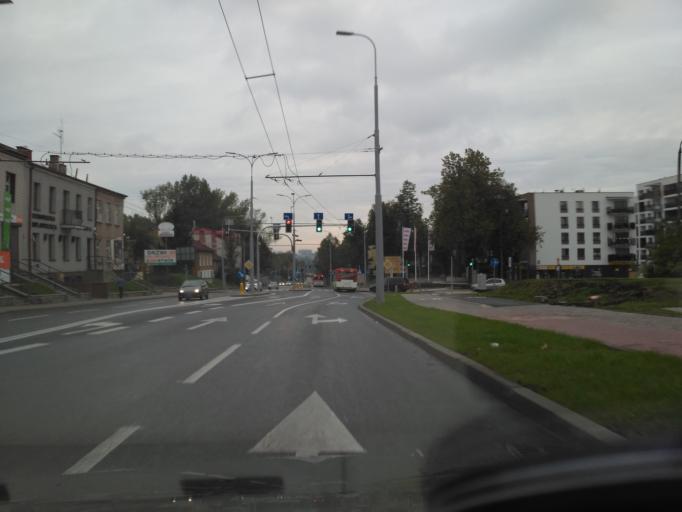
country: PL
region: Lublin Voivodeship
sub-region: Powiat lubelski
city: Lublin
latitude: 51.2335
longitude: 22.5854
